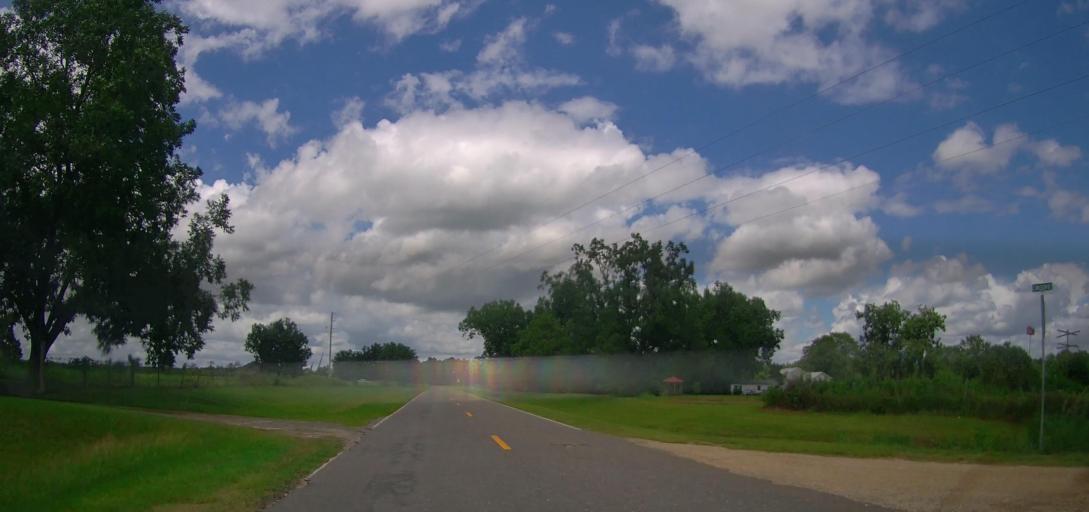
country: US
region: Georgia
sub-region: Ben Hill County
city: Fitzgerald
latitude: 31.6612
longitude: -83.4009
